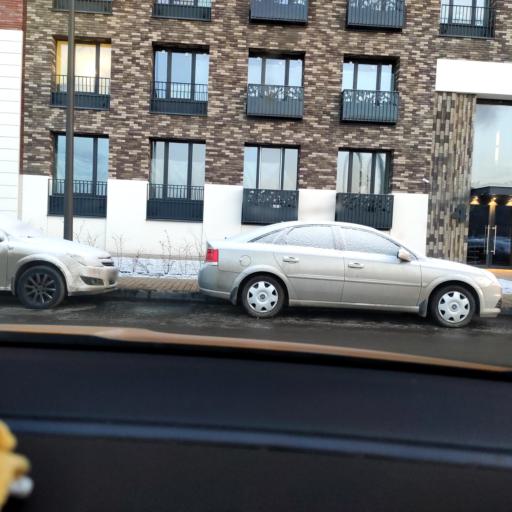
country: RU
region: Moskovskaya
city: Kur'yanovo
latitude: 55.6456
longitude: 37.7037
